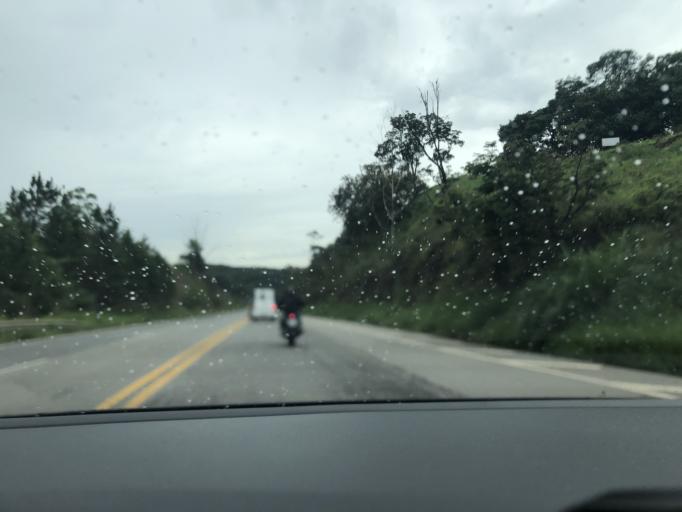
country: BR
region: Sao Paulo
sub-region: Jarinu
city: Jarinu
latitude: -23.1287
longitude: -46.7369
